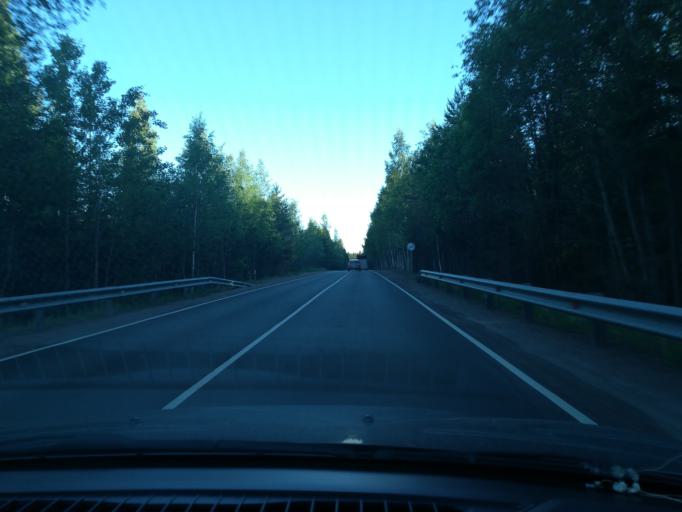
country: RU
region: Leningrad
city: Lesogorskiy
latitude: 60.9911
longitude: 28.9102
